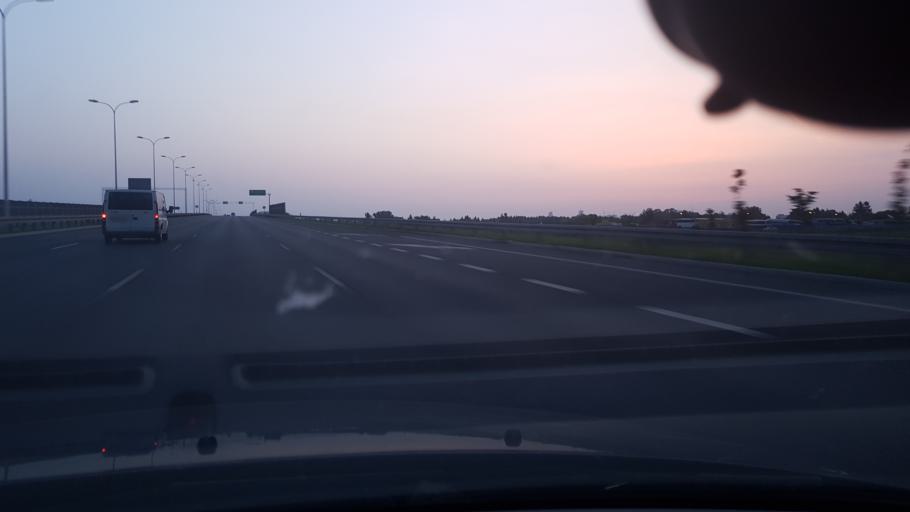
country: PL
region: Masovian Voivodeship
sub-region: Powiat pruszkowski
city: Nowe Grocholice
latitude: 52.1812
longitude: 20.9155
